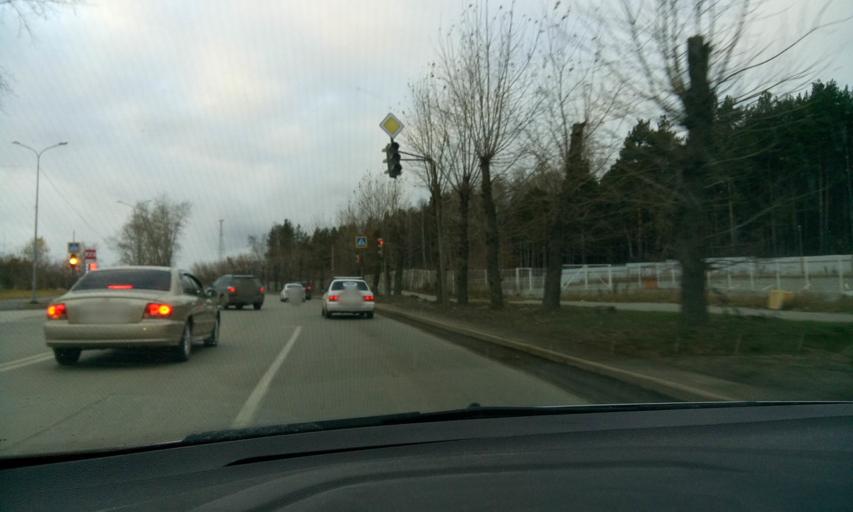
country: RU
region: Sverdlovsk
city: Yekaterinburg
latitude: 56.9128
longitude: 60.6186
